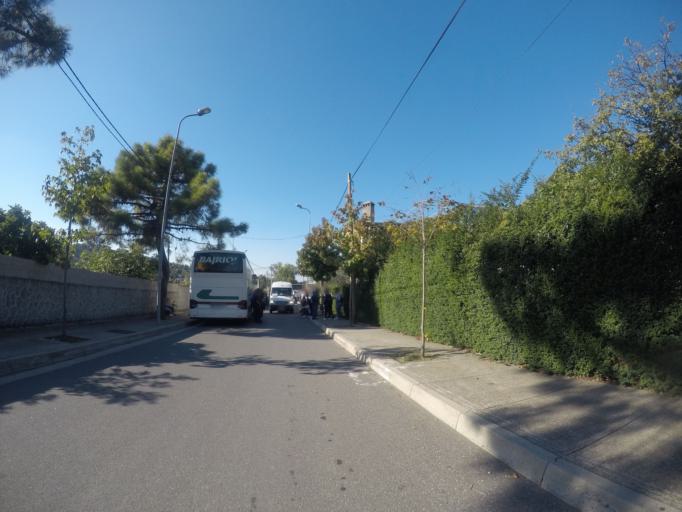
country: AL
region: Shkoder
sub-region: Rrethi i Shkodres
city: Shkoder
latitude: 42.0492
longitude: 19.4956
